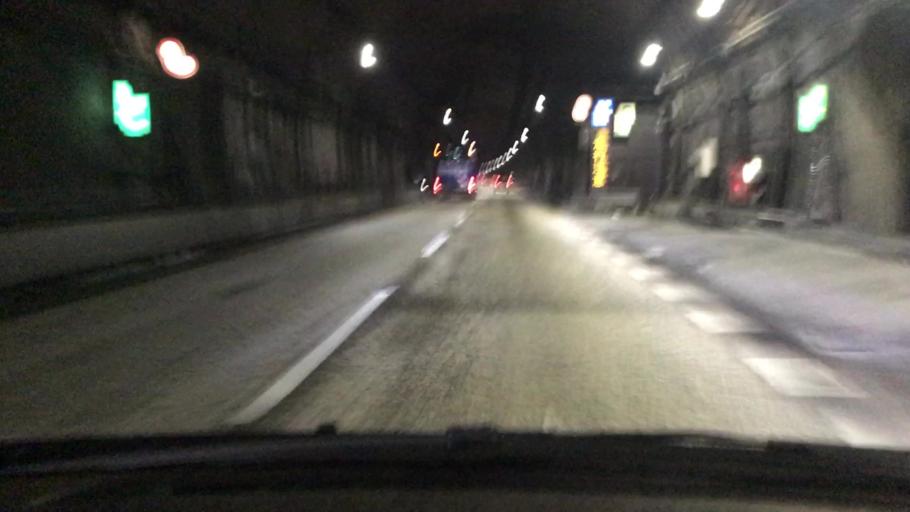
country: JP
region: Hyogo
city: Kobe
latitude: 34.7086
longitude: 135.1938
